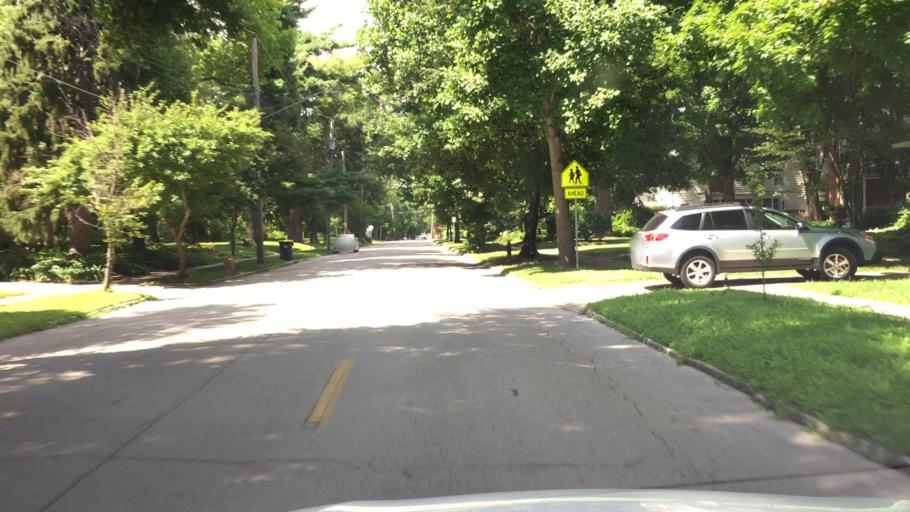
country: US
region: Iowa
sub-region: Johnson County
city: Iowa City
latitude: 41.6527
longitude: -91.5212
